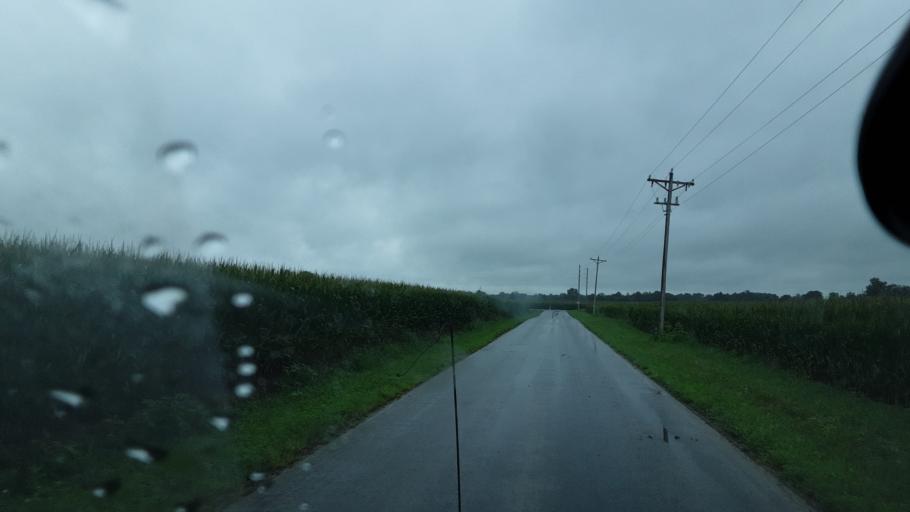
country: US
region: Indiana
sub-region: Adams County
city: Decatur
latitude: 40.7589
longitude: -84.8575
